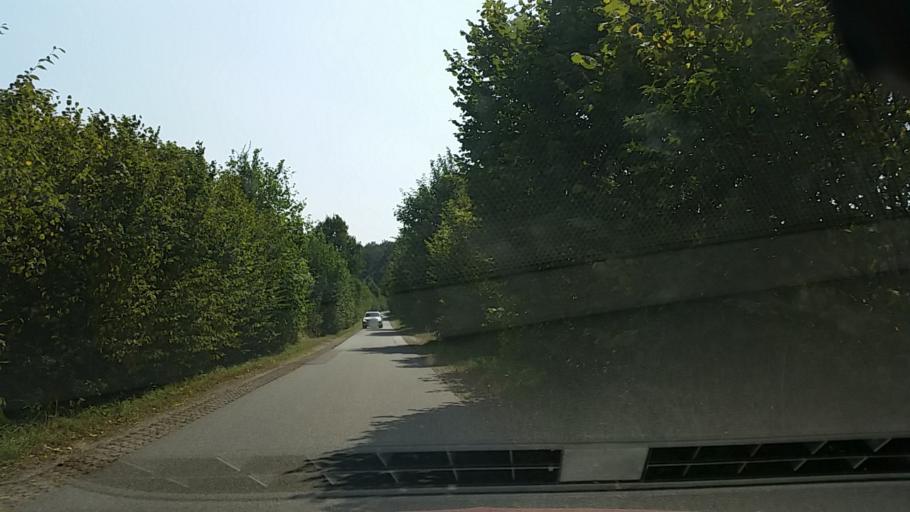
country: DE
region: Schleswig-Holstein
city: Borstorf
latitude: 53.6250
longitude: 10.5710
